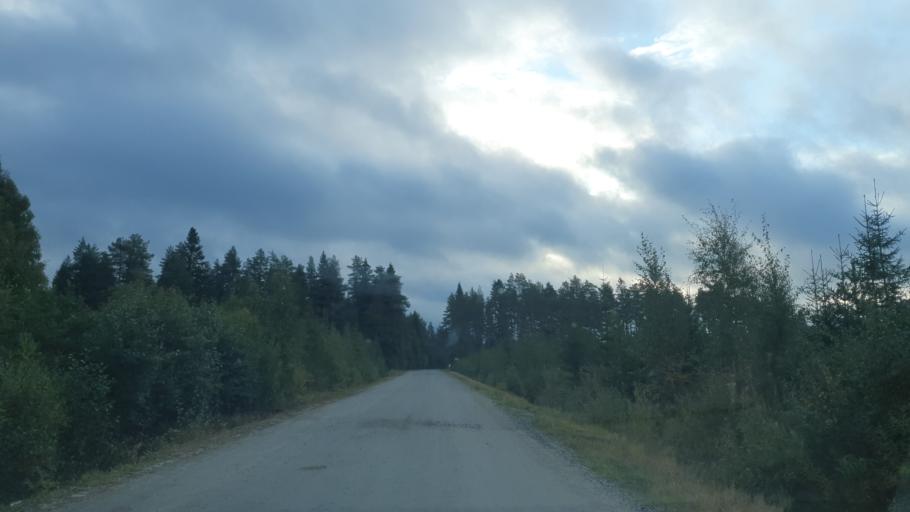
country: FI
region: Kainuu
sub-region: Kehys-Kainuu
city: Kuhmo
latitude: 64.1341
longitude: 29.5749
